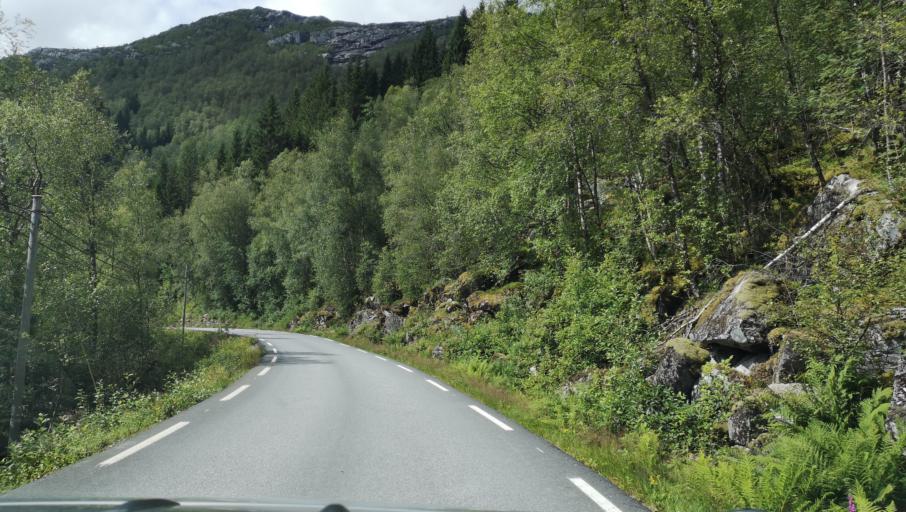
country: NO
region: Hordaland
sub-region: Modalen
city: Mo
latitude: 60.7857
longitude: 5.9411
